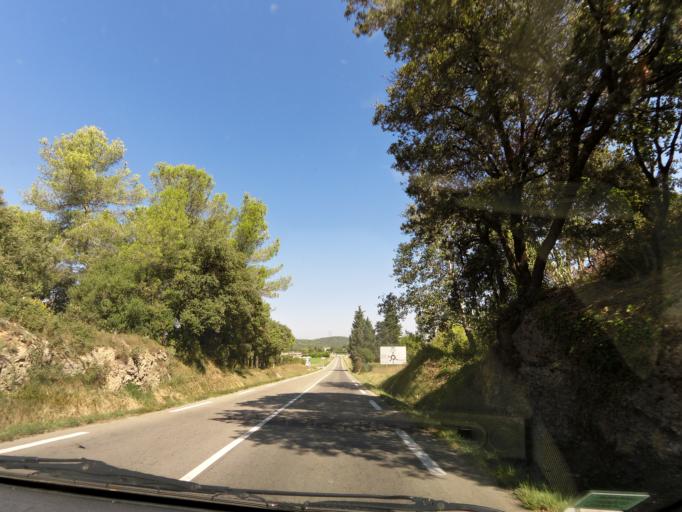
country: FR
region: Languedoc-Roussillon
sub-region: Departement du Gard
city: Villevieille
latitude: 43.8244
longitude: 4.0955
